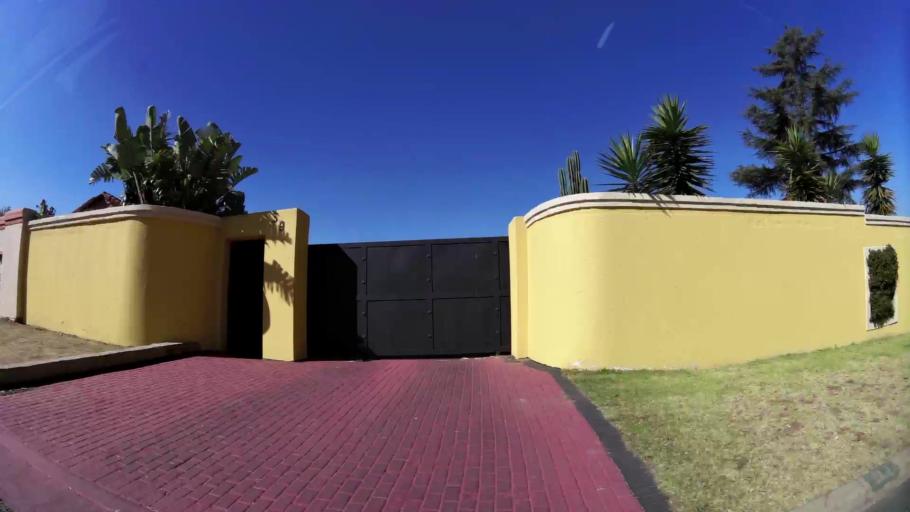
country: ZA
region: Gauteng
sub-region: Ekurhuleni Metropolitan Municipality
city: Tembisa
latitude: -26.0370
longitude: 28.2327
